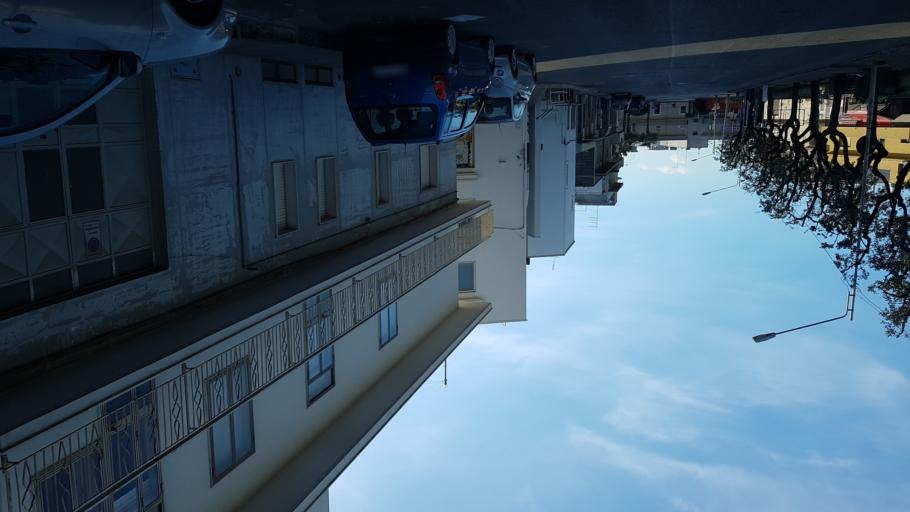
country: IT
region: Apulia
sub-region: Provincia di Brindisi
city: Carovigno
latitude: 40.7052
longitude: 17.6635
